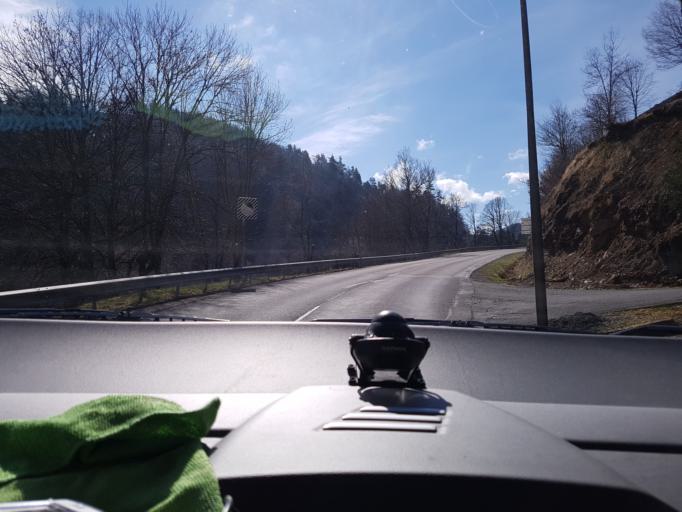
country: FR
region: Auvergne
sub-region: Departement du Cantal
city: Chaudes-Aigues
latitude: 44.8497
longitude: 3.0017
